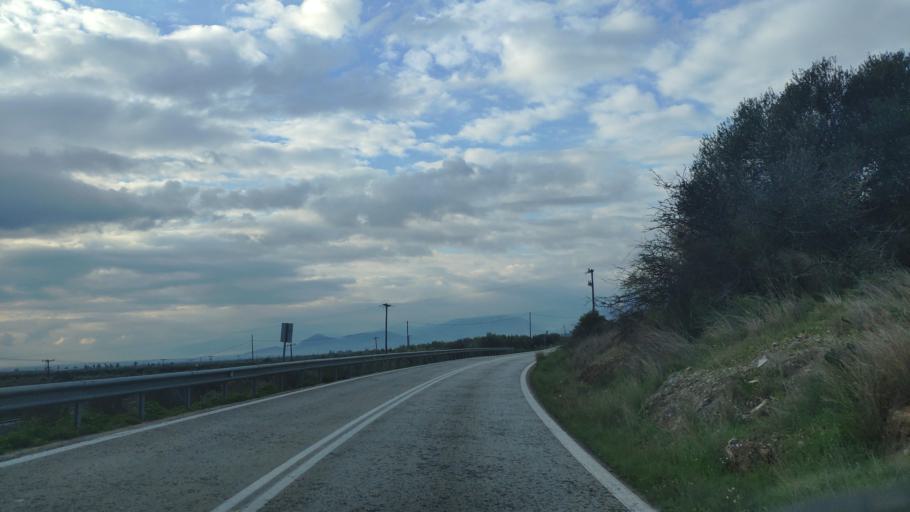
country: GR
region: Peloponnese
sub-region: Nomos Argolidos
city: Koutsopodi
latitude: 37.7331
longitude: 22.7357
